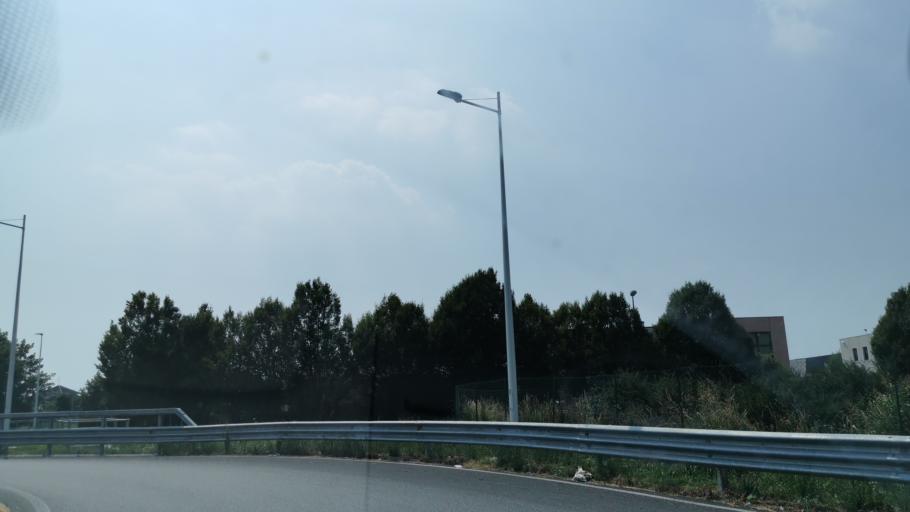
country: IT
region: Lombardy
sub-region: Provincia di Bergamo
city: Orio al Serio
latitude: 45.6594
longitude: 9.7035
